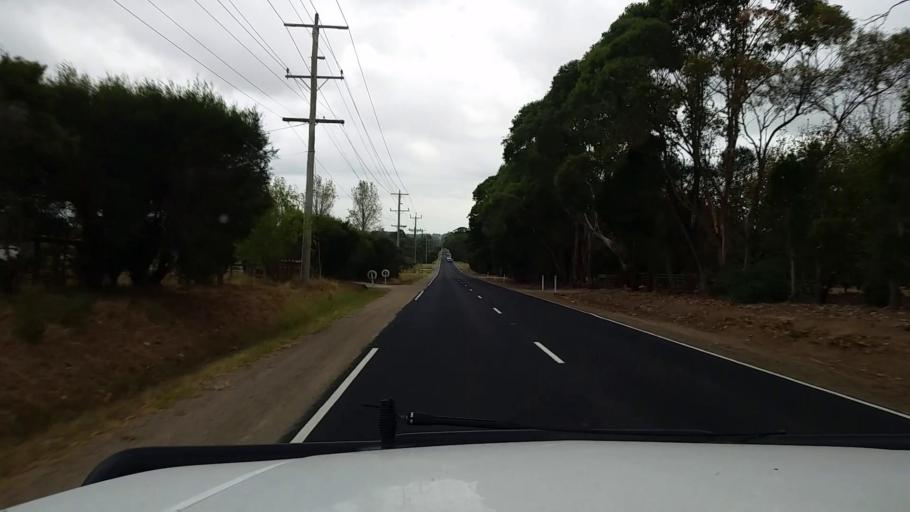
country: AU
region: Victoria
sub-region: Mornington Peninsula
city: Somerville
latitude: -38.2175
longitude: 145.1556
